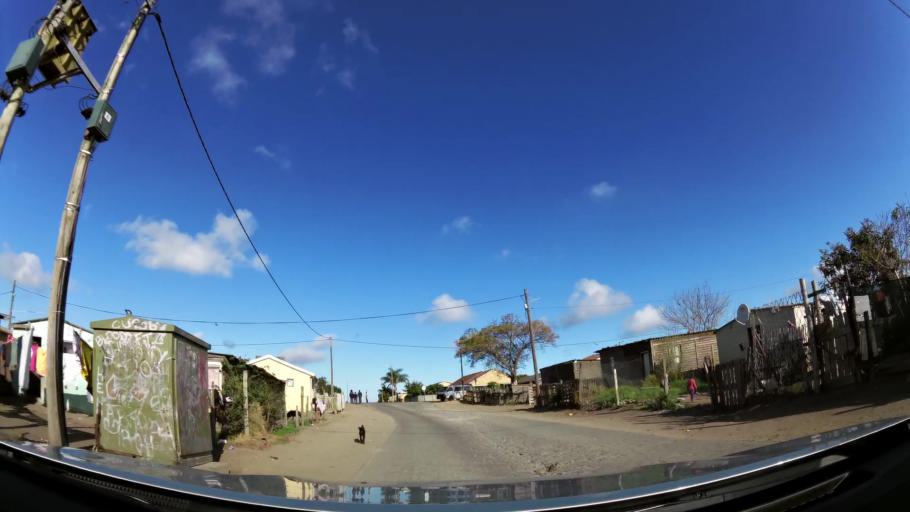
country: ZA
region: Western Cape
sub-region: Eden District Municipality
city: George
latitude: -33.9893
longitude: 22.4795
